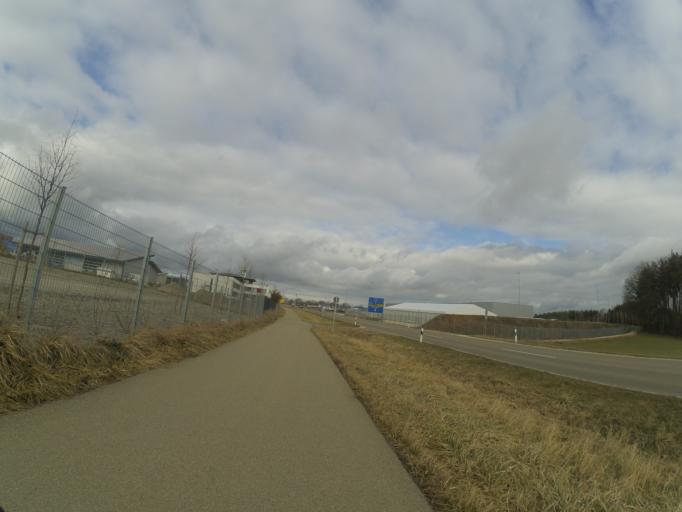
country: DE
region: Bavaria
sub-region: Swabia
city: Vohringen
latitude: 48.2835
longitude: 10.1178
